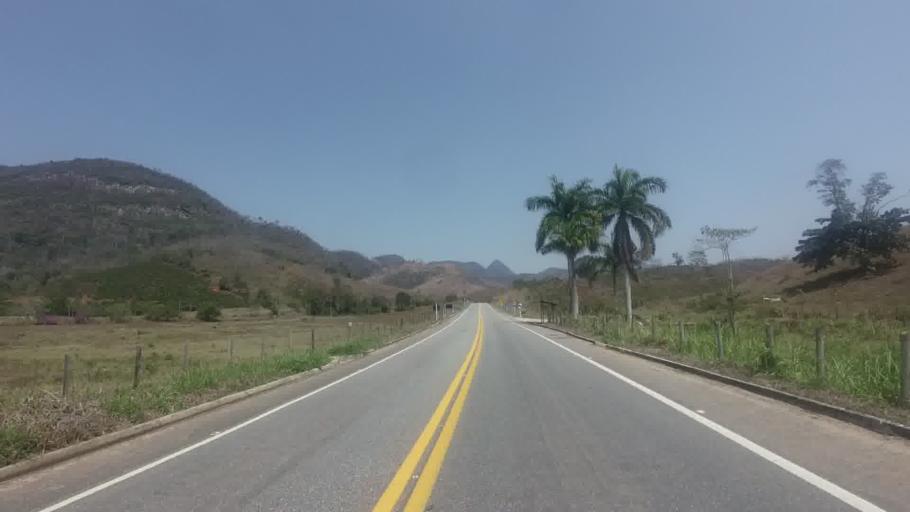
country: BR
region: Espirito Santo
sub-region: Jeronimo Monteiro
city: Jeronimo Monteiro
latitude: -20.9126
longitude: -41.3028
